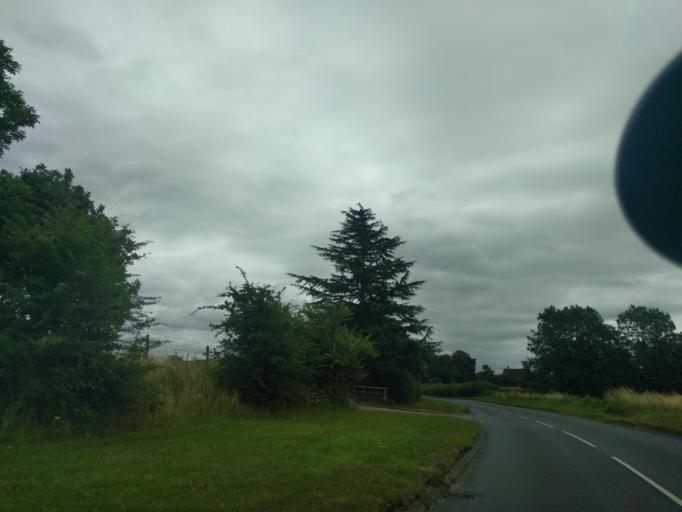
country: GB
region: England
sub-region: Wiltshire
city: Erlestoke
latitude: 51.2801
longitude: -2.0272
